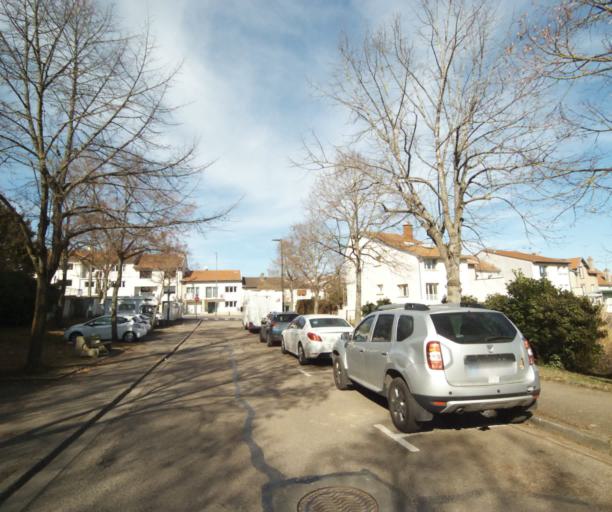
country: FR
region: Lorraine
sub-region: Departement de Meurthe-et-Moselle
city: Villers-les-Nancy
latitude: 48.6728
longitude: 6.1490
